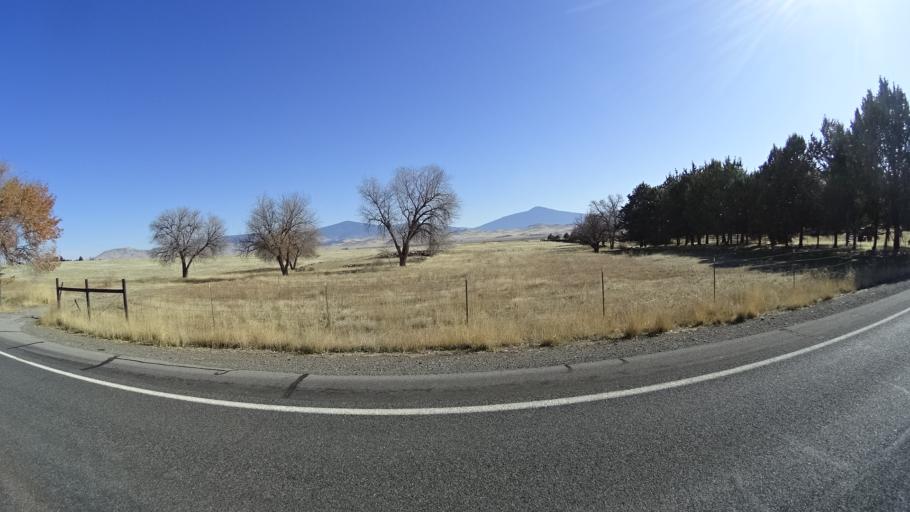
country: US
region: California
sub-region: Siskiyou County
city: Montague
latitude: 41.7643
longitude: -122.5247
